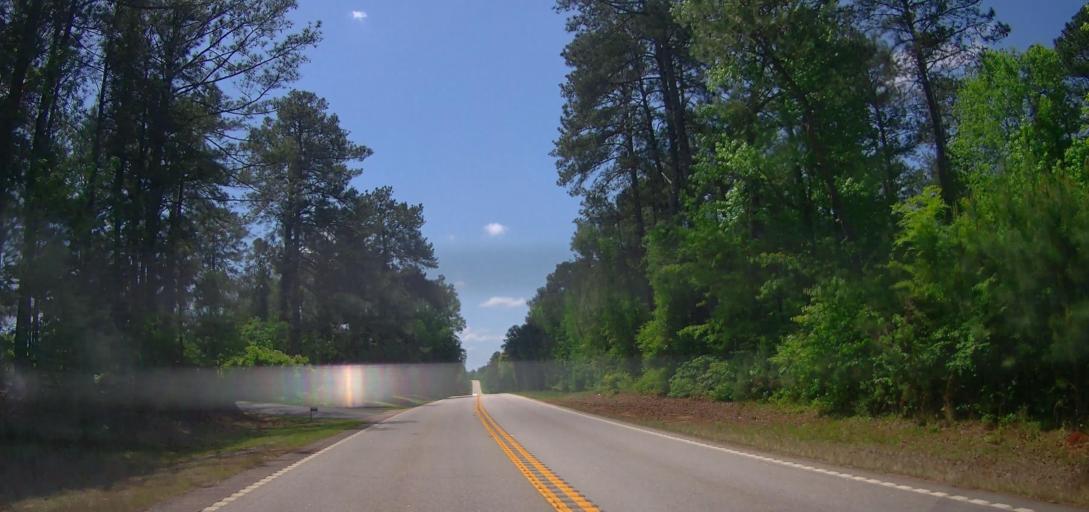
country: US
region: Georgia
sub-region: Jasper County
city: Monticello
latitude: 33.2527
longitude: -83.6749
